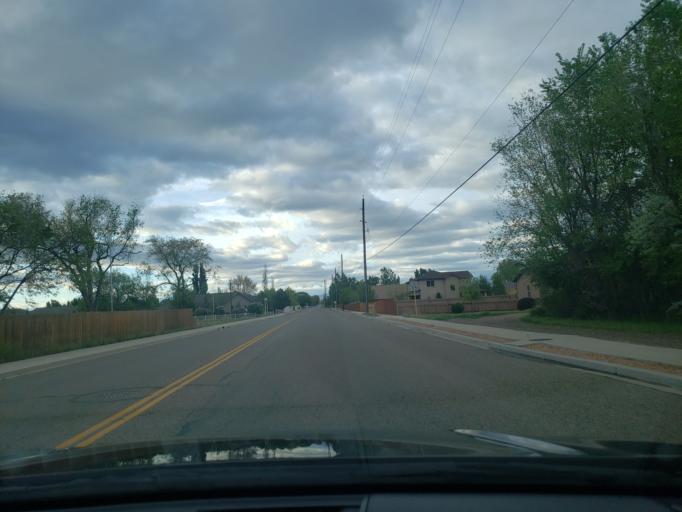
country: US
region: Colorado
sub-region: Mesa County
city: Fruita
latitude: 39.1712
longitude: -108.7290
